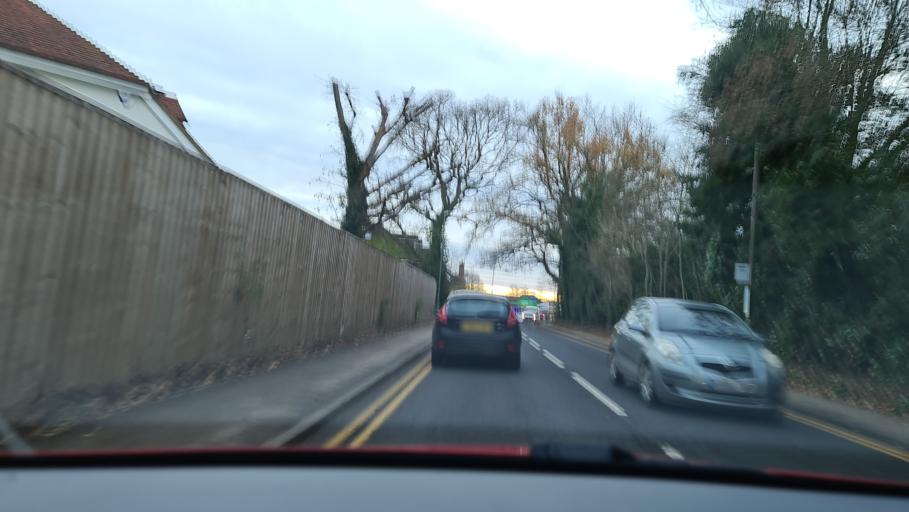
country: GB
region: England
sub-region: Buckinghamshire
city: Amersham on the Hill
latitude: 51.6819
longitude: -0.6098
